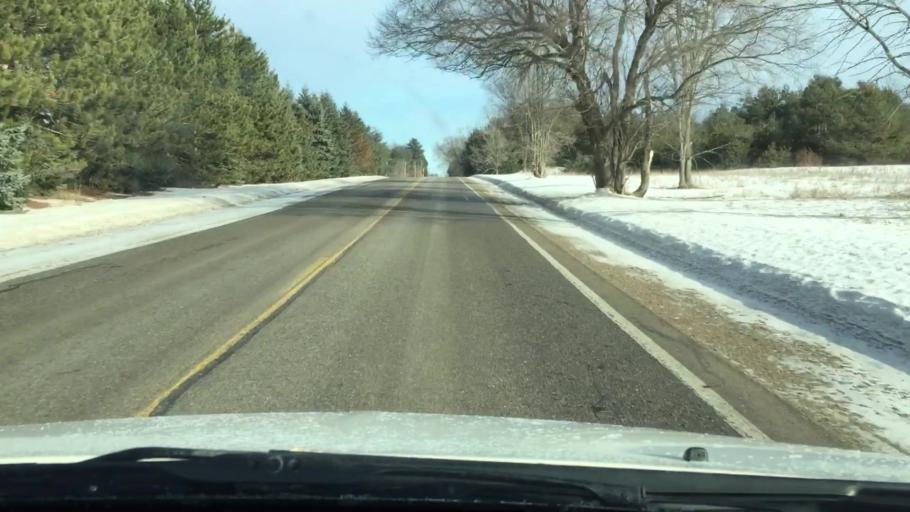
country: US
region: Michigan
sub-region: Kalkaska County
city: Kalkaska
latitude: 44.6408
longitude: -85.2379
